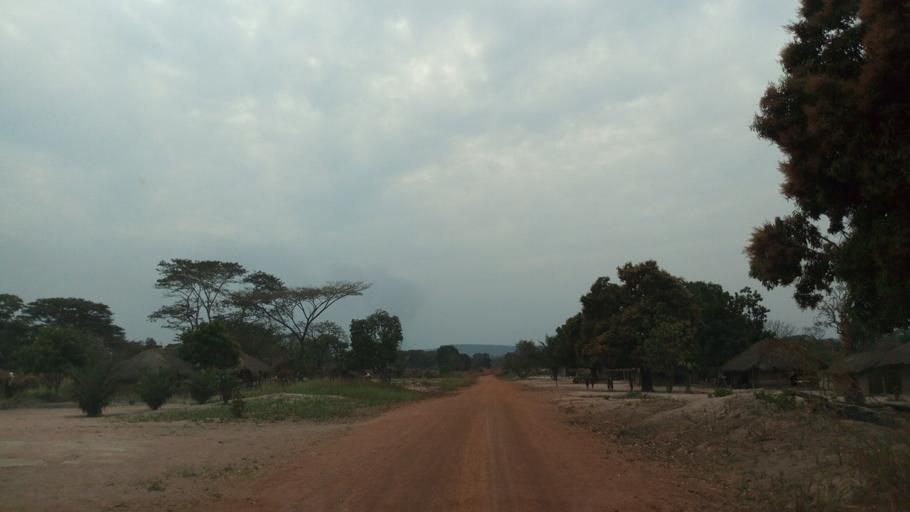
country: ZM
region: Northern
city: Kaputa
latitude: -8.1667
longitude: 29.0945
